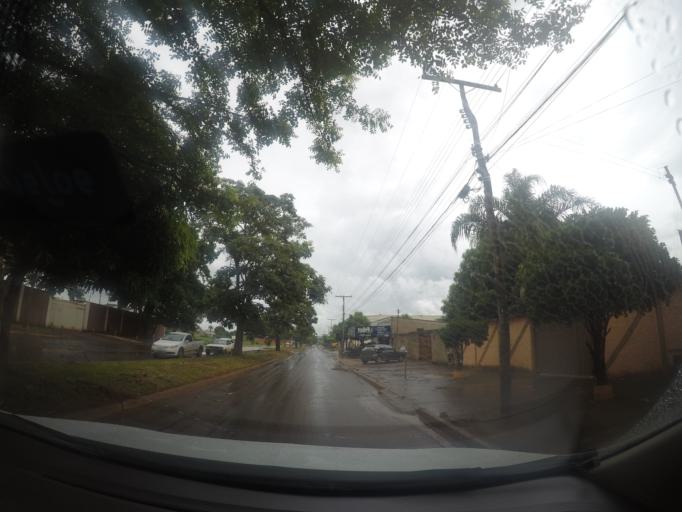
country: BR
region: Goias
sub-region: Trindade
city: Trindade
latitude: -16.6439
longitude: -49.4343
